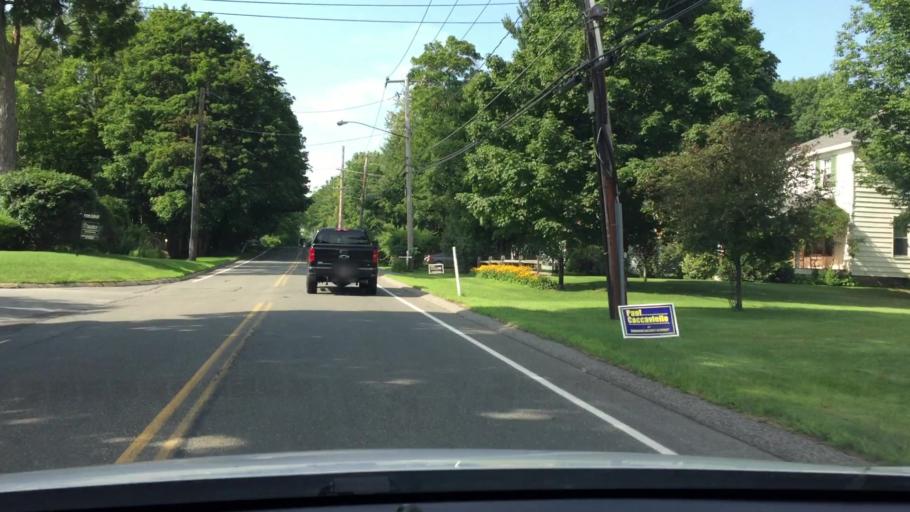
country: US
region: Massachusetts
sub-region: Berkshire County
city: Pittsfield
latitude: 42.4205
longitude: -73.2458
